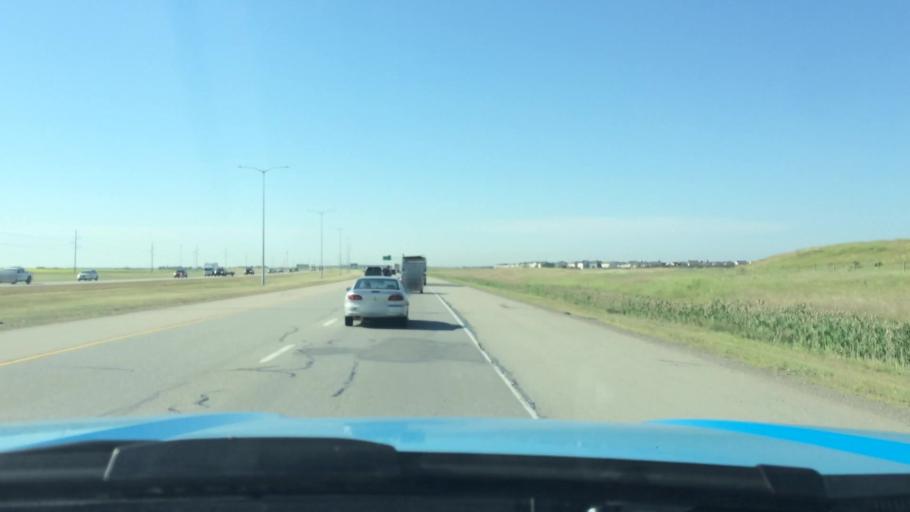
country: CA
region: Alberta
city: Chestermere
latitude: 51.1175
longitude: -113.9216
